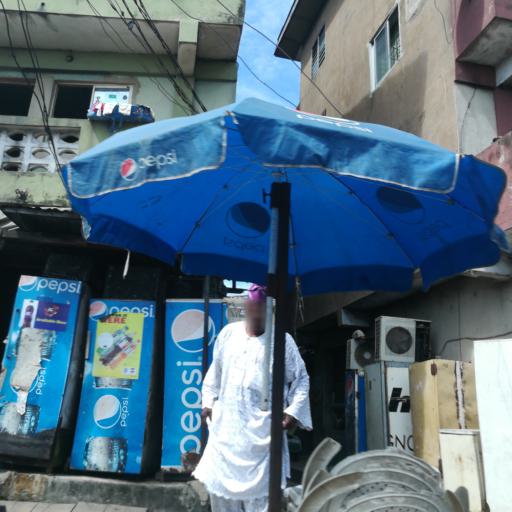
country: NG
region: Lagos
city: Lagos
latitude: 6.4652
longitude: 3.3909
